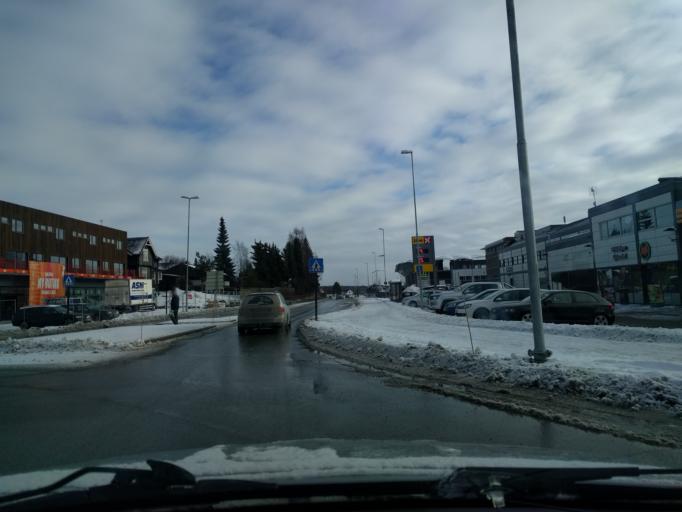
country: NO
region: Hedmark
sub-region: Hamar
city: Hamar
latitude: 60.7968
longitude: 11.0883
